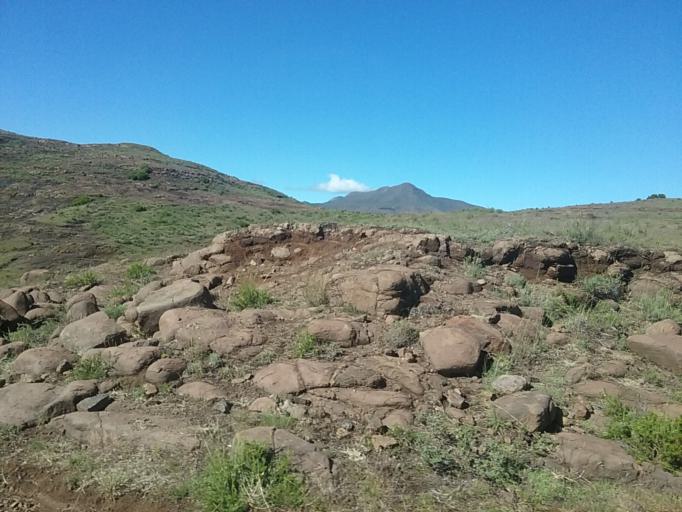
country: LS
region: Berea
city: Teyateyaneng
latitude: -29.2371
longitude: 27.9102
